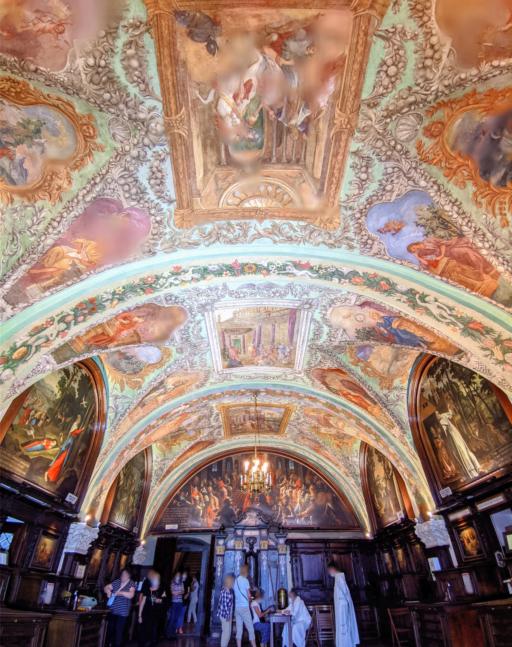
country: PL
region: Silesian Voivodeship
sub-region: Czestochowa
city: Czestochowa
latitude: 50.8125
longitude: 19.0981
